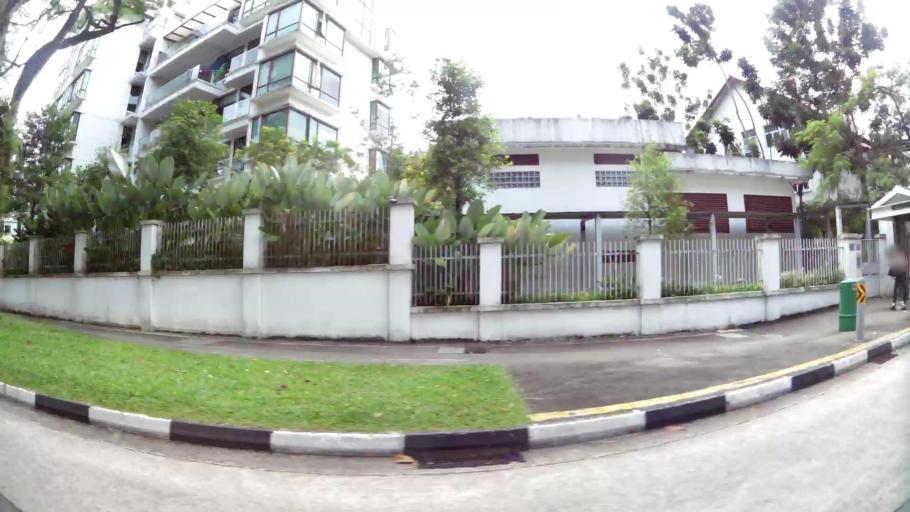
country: SG
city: Singapore
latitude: 1.3470
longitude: 103.7647
